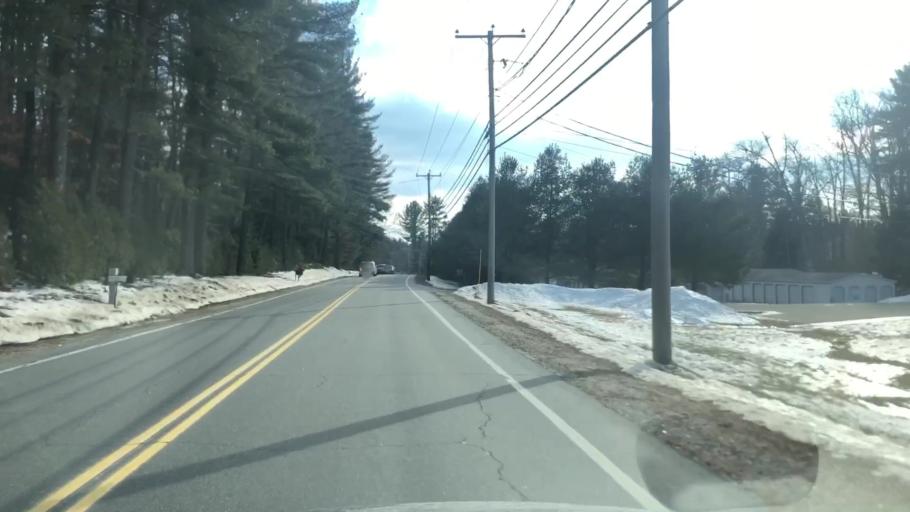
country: US
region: New Hampshire
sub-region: Hillsborough County
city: Milford
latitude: 42.8503
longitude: -71.6626
